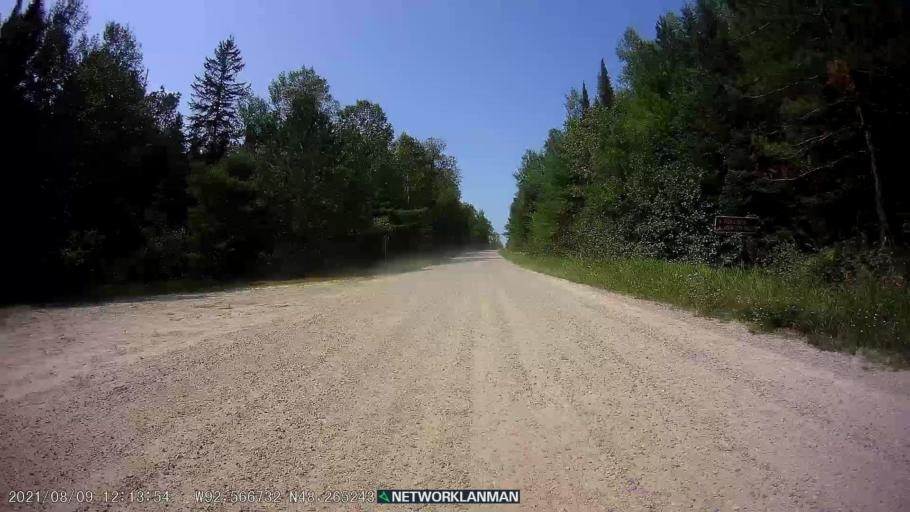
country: US
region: Minnesota
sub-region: Saint Louis County
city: Parkville
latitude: 48.2652
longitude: -92.5666
